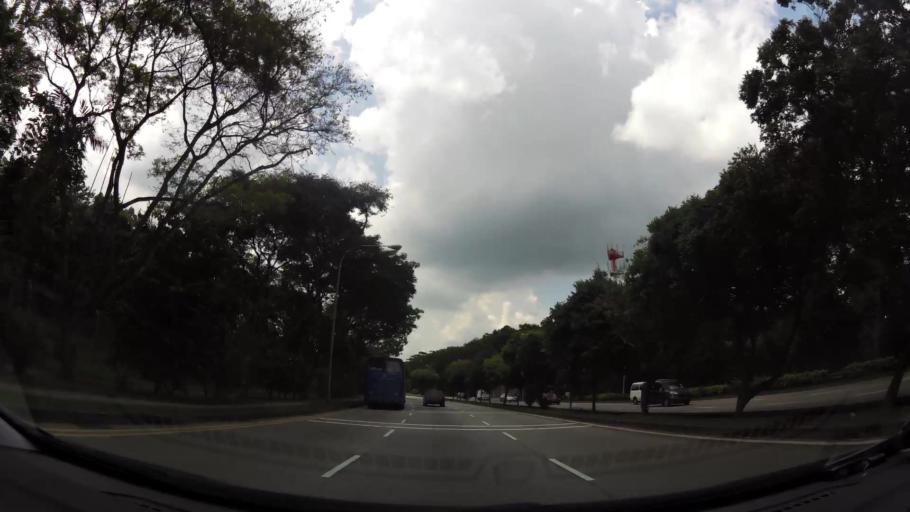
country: MY
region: Johor
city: Johor Bahru
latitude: 1.4153
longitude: 103.8096
